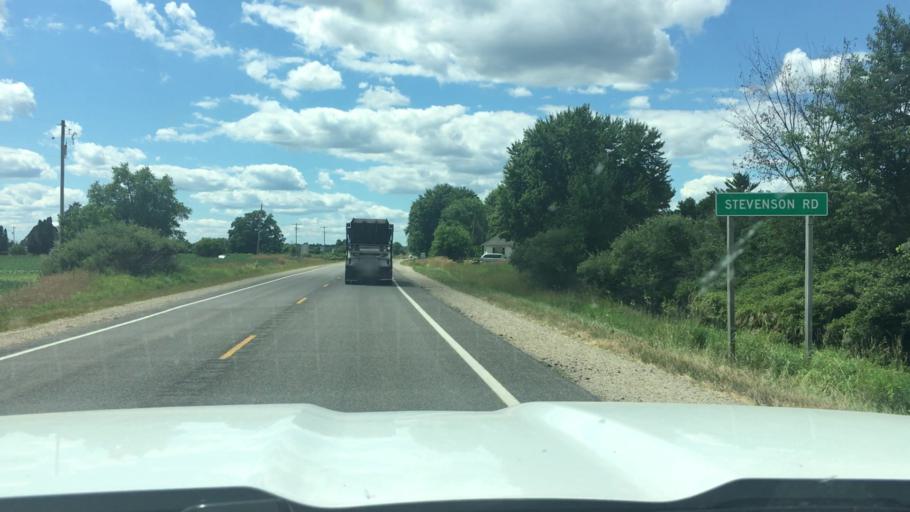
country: US
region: Michigan
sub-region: Montcalm County
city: Stanton
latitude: 43.1775
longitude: -85.0317
